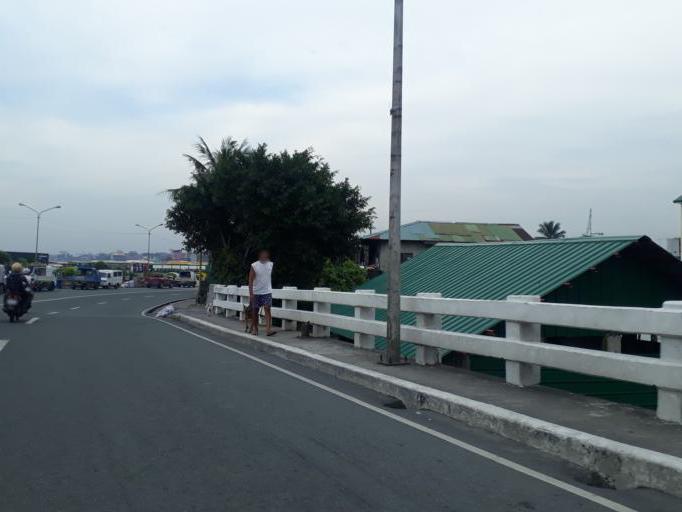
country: PH
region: Metro Manila
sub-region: Caloocan City
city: Niugan
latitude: 14.6502
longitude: 120.9482
